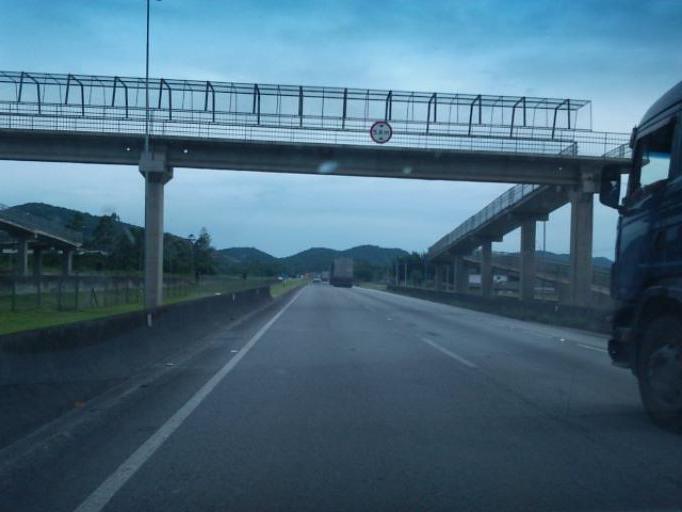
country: BR
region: Sao Paulo
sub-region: Juquia
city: Juquia
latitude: -24.3385
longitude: -47.6442
